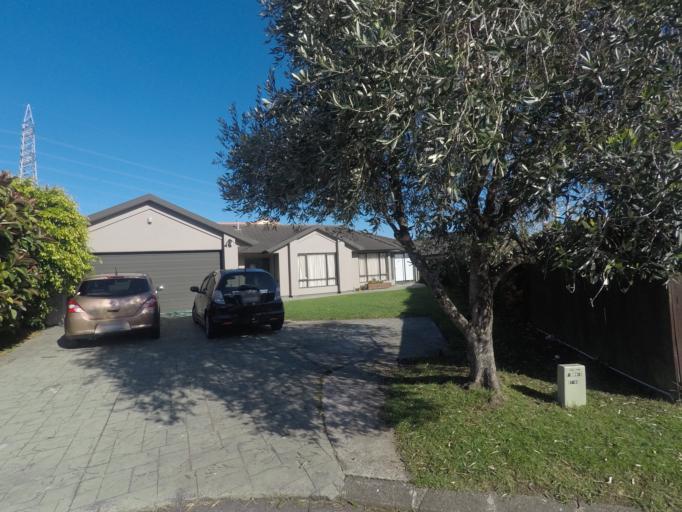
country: NZ
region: Auckland
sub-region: Auckland
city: Rosebank
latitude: -36.8994
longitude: 174.6858
